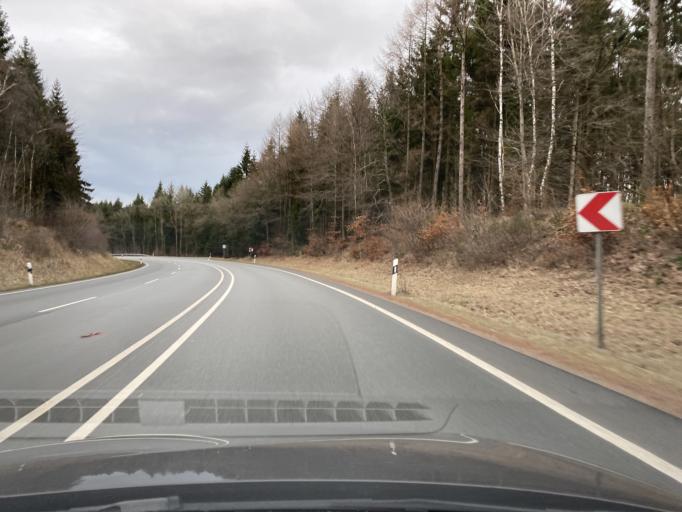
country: DE
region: North Rhine-Westphalia
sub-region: Regierungsbezirk Arnsberg
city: Meschede
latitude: 51.3962
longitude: 8.3164
